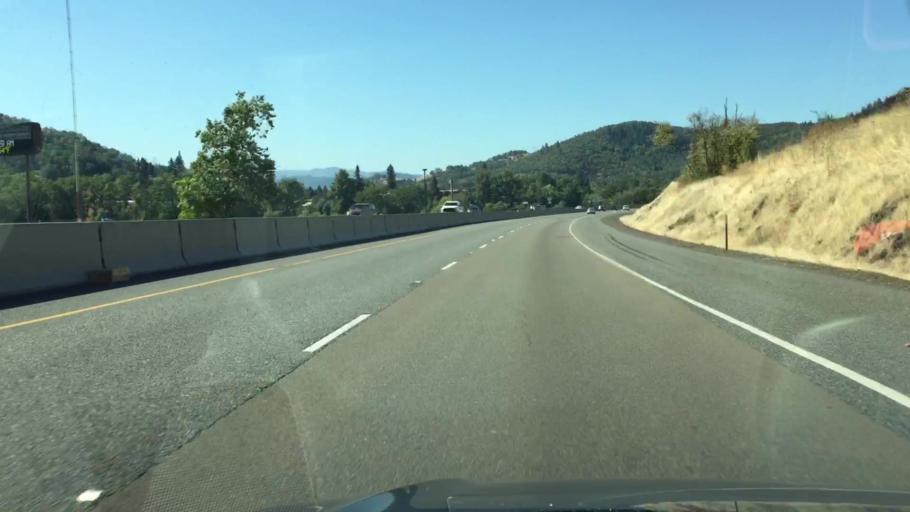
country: US
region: Oregon
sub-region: Douglas County
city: Roseburg
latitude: 43.1960
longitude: -123.3618
